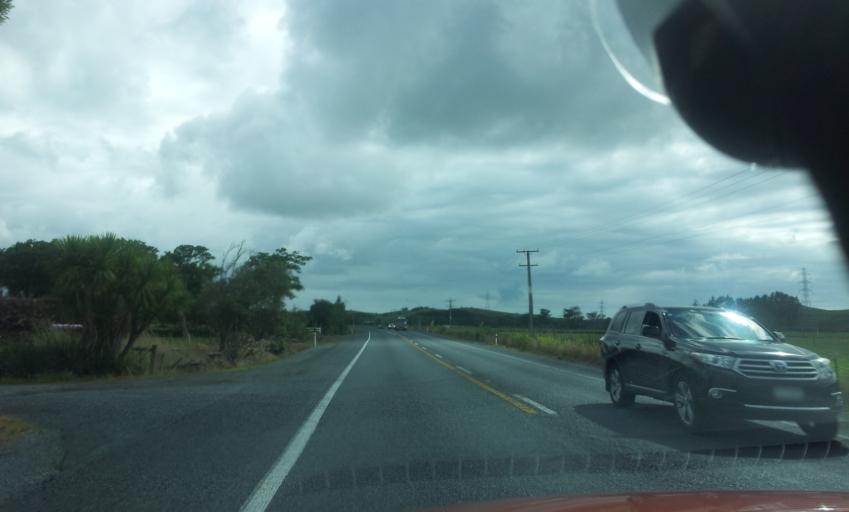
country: NZ
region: Northland
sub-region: Whangarei
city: Ruakaka
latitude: -36.0224
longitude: 174.4181
